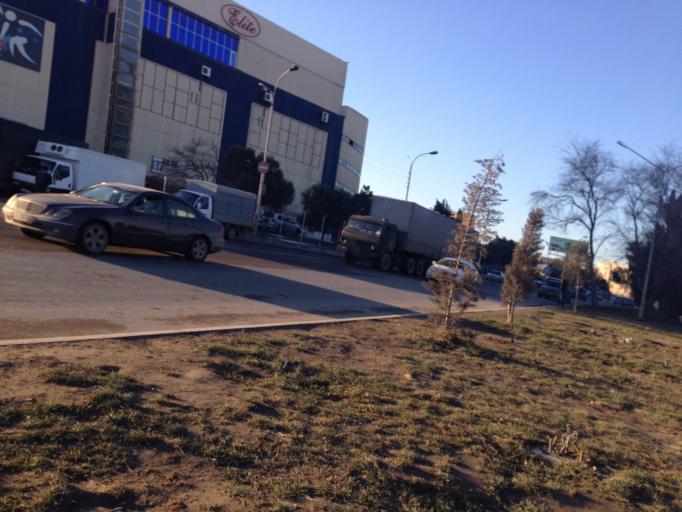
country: AZ
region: Baki
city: Binagadi
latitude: 40.4195
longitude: 49.8558
